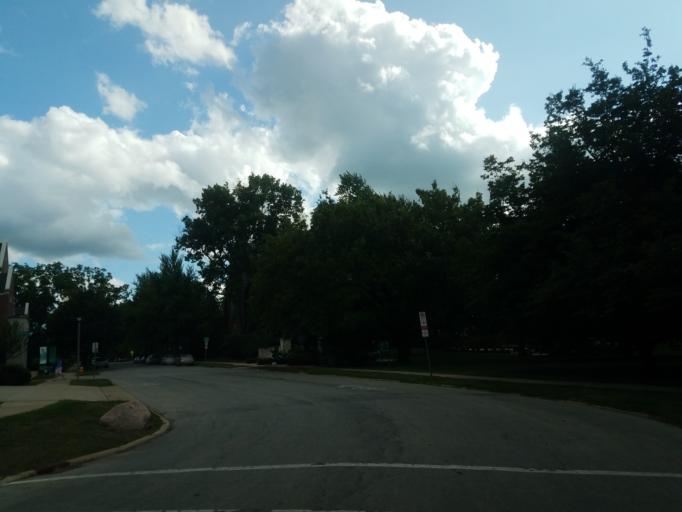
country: US
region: Illinois
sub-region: McLean County
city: Bloomington
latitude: 40.4907
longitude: -88.9900
